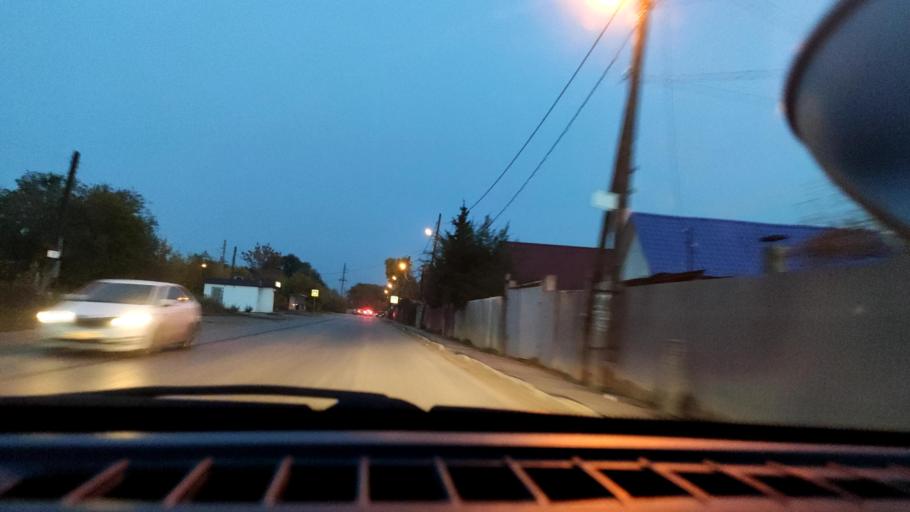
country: RU
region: Samara
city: Samara
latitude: 53.1355
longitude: 50.1169
